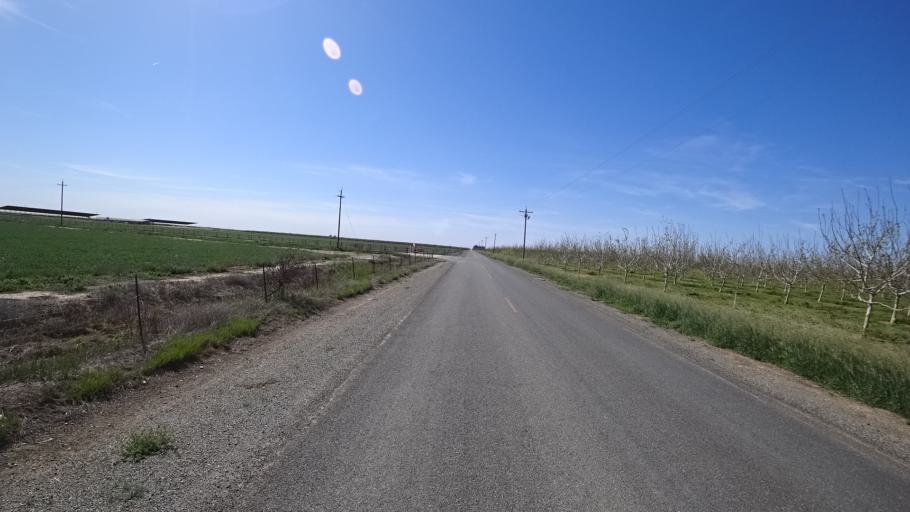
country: US
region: California
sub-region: Glenn County
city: Hamilton City
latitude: 39.6774
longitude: -122.1033
